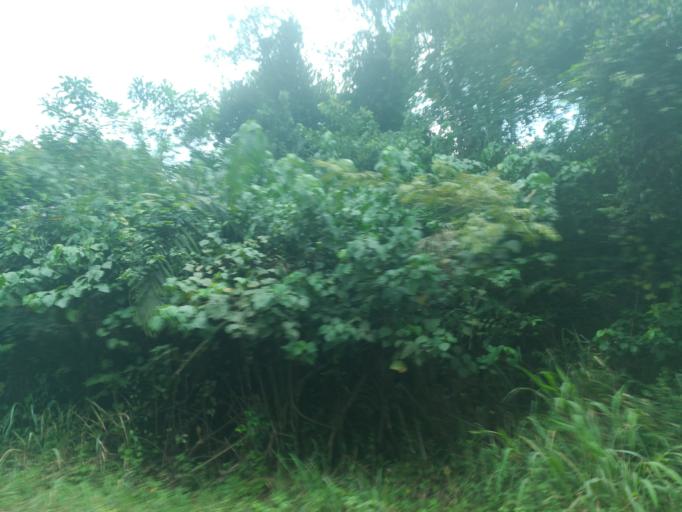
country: NG
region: Lagos
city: Ikorodu
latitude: 6.6719
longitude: 3.6463
